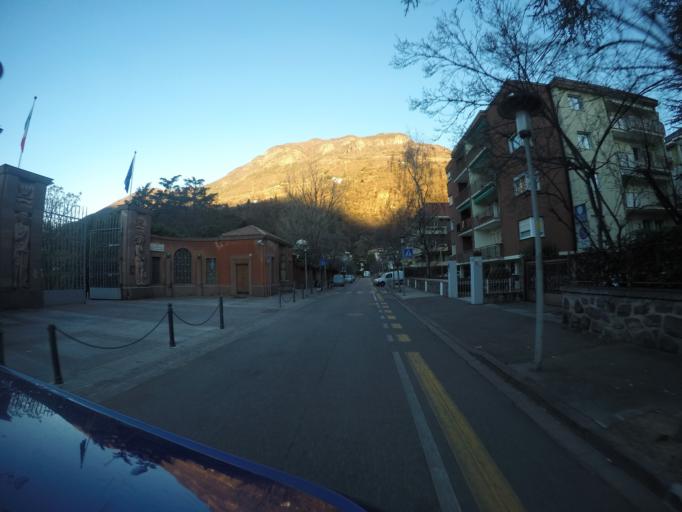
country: IT
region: Trentino-Alto Adige
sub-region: Bolzano
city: Bolzano
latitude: 46.5056
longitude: 11.3396
